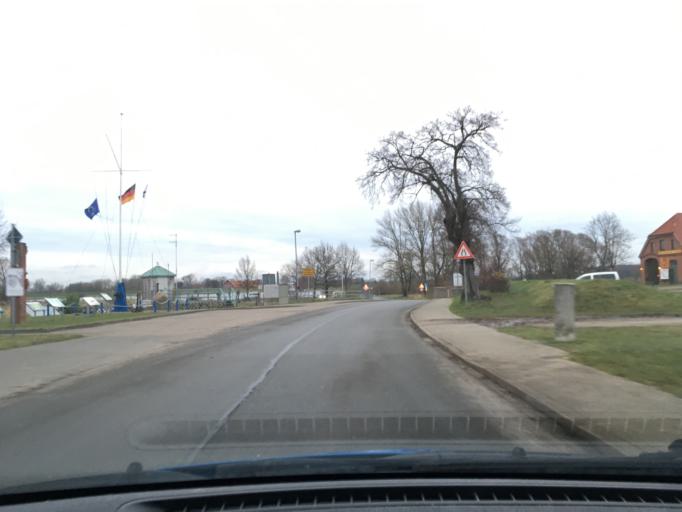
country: DE
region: Lower Saxony
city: Neu Darchau
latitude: 53.2317
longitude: 10.8884
